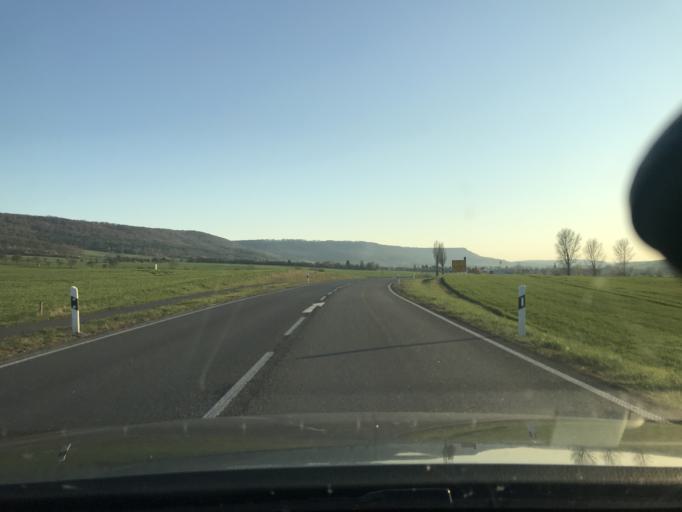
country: DE
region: Thuringia
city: Niedergebra
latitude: 51.4275
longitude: 10.6211
